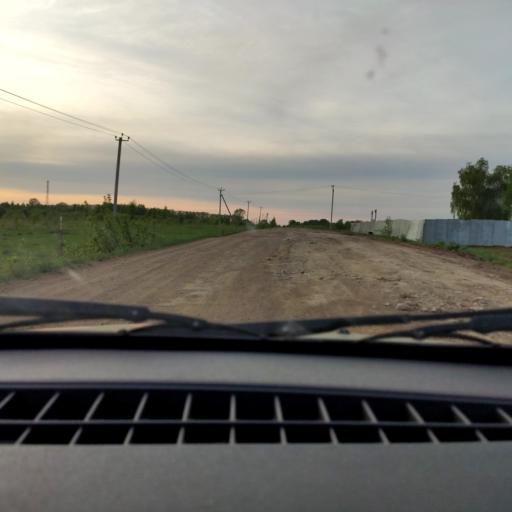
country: RU
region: Bashkortostan
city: Iglino
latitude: 54.8496
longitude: 56.4003
